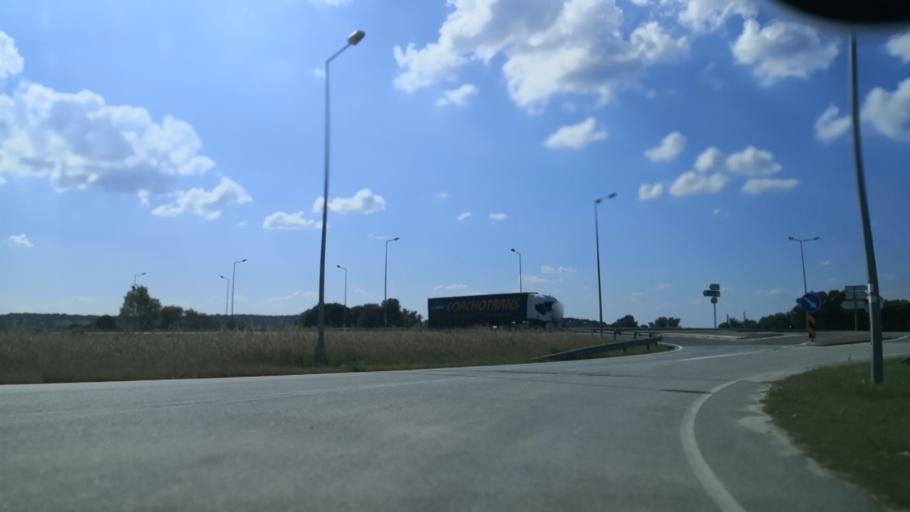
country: PT
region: Evora
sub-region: Arraiolos
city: Arraiolos
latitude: 38.7008
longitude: -8.0646
